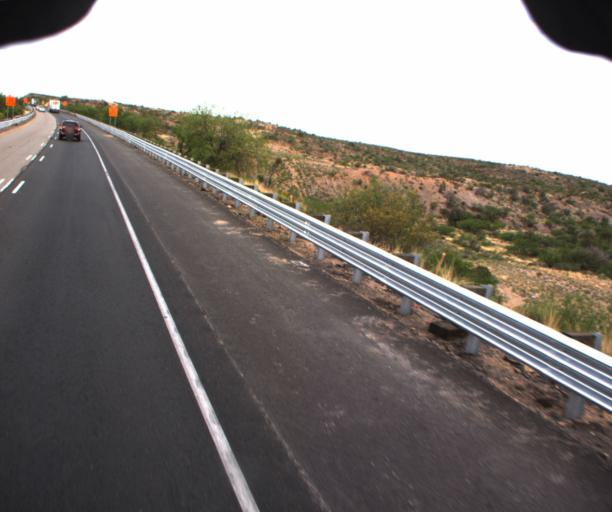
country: US
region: Arizona
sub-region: Pima County
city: Vail
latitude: 31.9990
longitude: -110.6307
